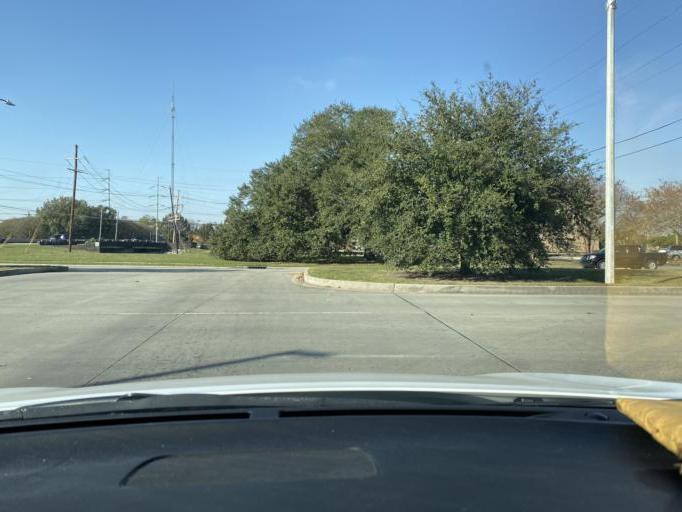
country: US
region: Louisiana
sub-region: Jefferson Parish
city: Terrytown
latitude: 29.9222
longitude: -90.0139
